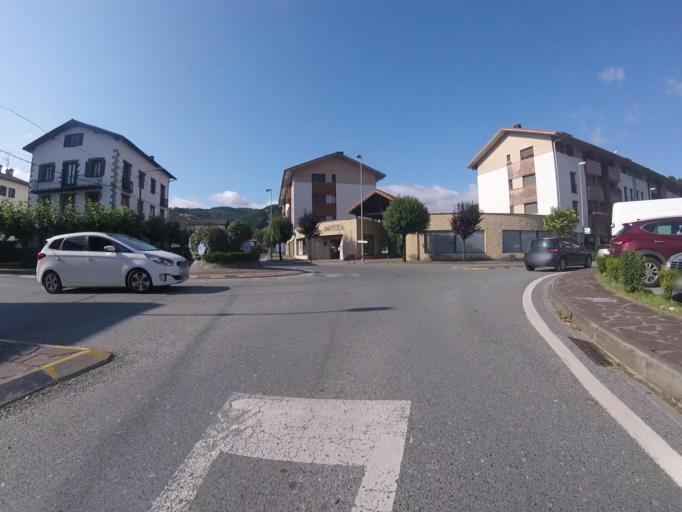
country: ES
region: Navarre
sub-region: Provincia de Navarra
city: Bera
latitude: 43.2750
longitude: -1.6883
